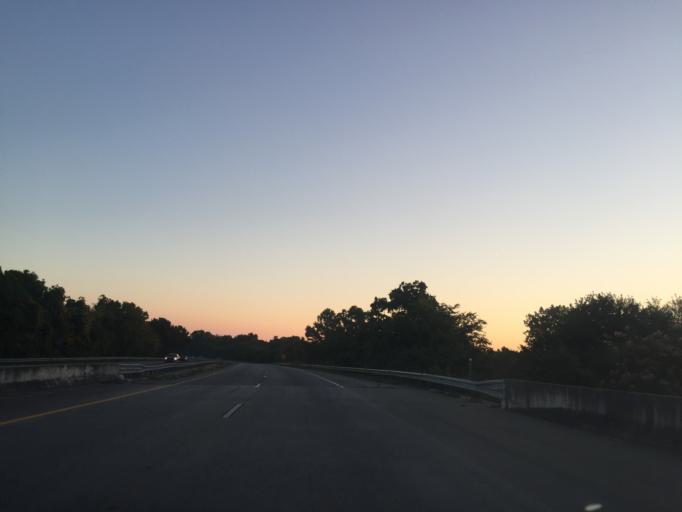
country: US
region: Georgia
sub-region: Chatham County
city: Thunderbolt
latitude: 32.0438
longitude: -81.0695
